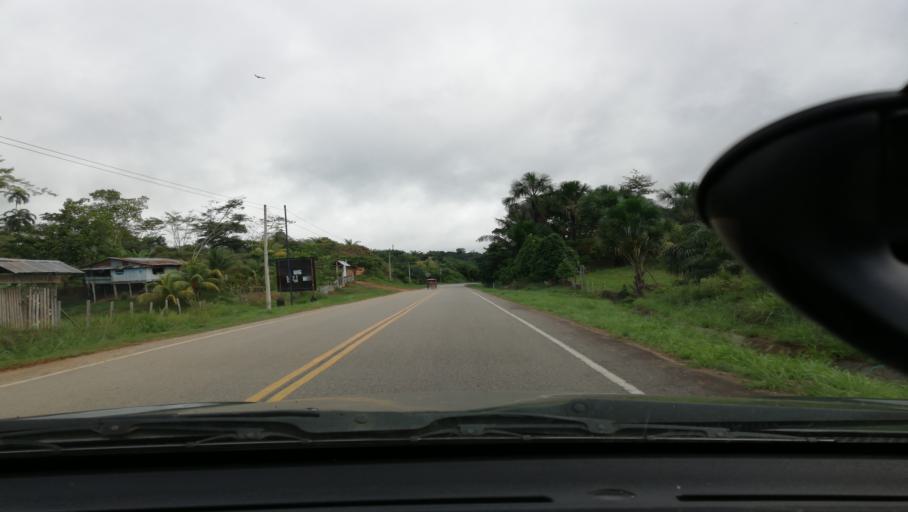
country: PE
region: Loreto
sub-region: Provincia de Loreto
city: Nauta
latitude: -4.4927
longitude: -73.5970
